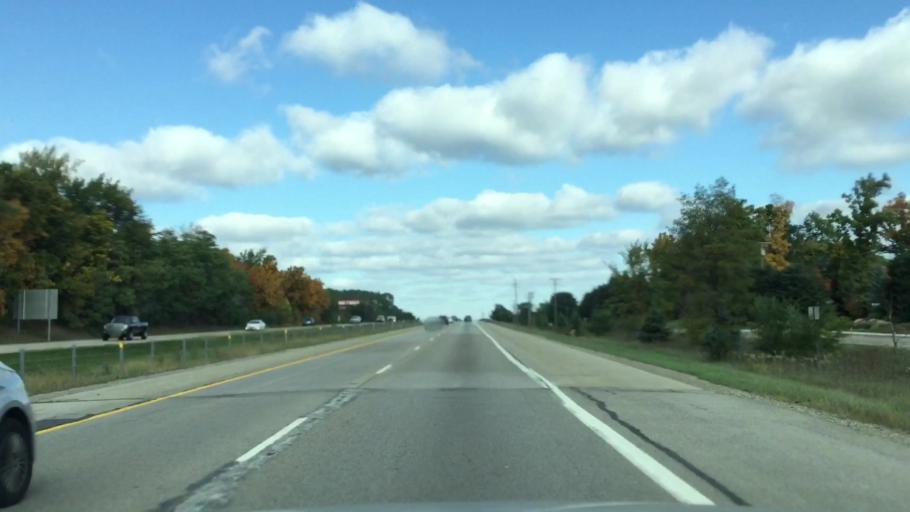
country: US
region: Michigan
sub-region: Livingston County
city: Brighton
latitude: 42.6403
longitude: -83.7517
